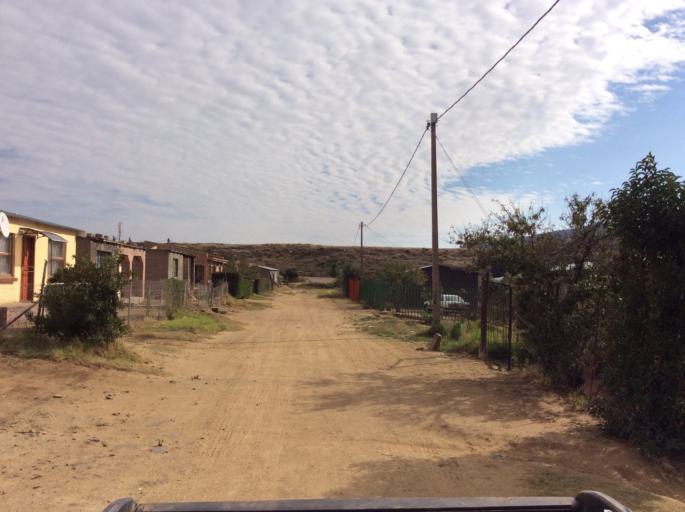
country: LS
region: Mafeteng
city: Mafeteng
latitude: -29.7183
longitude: 27.0182
